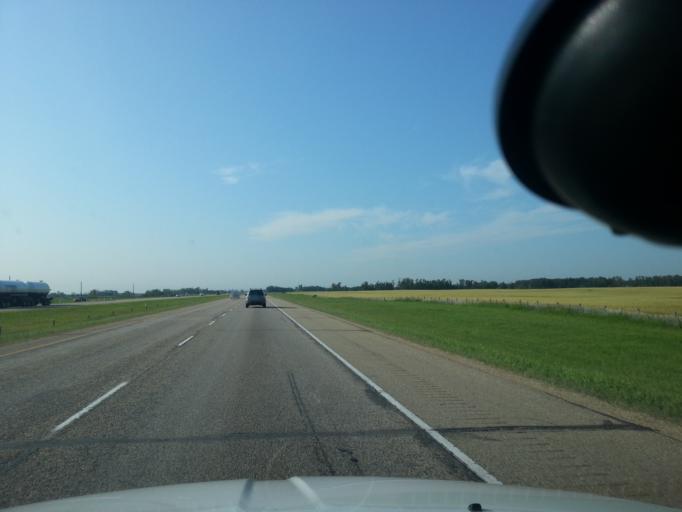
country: CA
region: Alberta
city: Ponoka
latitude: 52.8944
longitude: -113.6442
